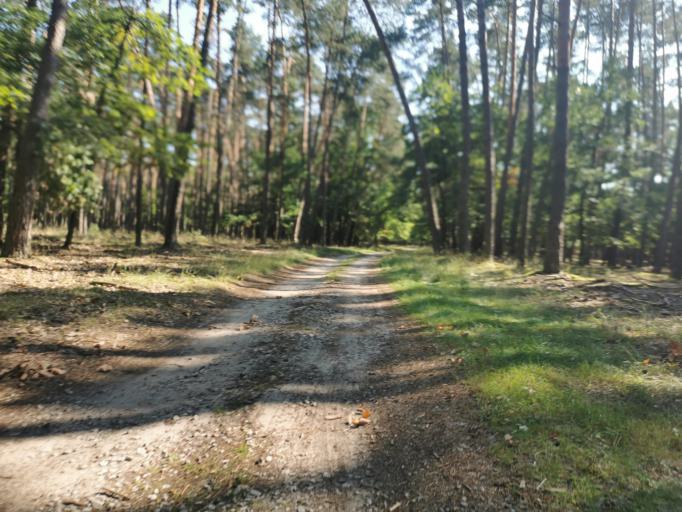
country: SK
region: Trnavsky
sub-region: Okres Senica
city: Senica
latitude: 48.6388
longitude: 17.2783
